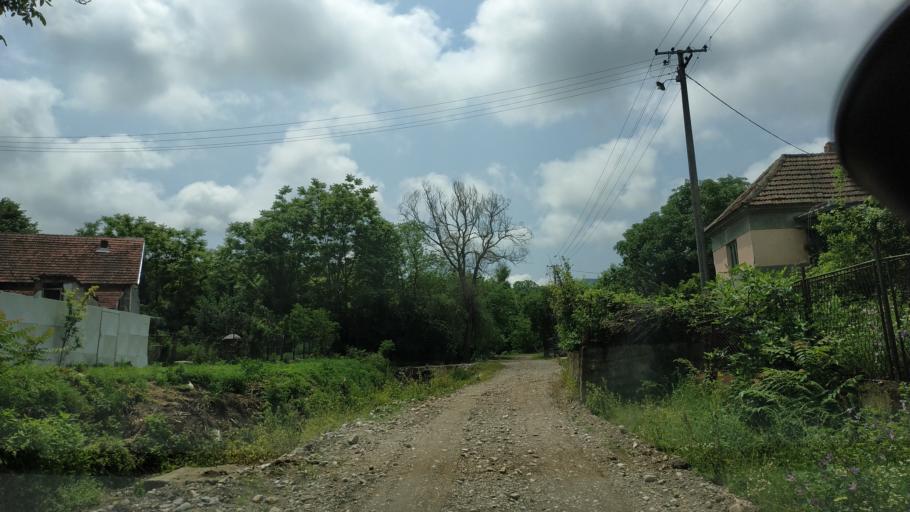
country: RS
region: Central Serbia
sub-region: Nisavski Okrug
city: Aleksinac
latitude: 43.4202
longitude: 21.7012
